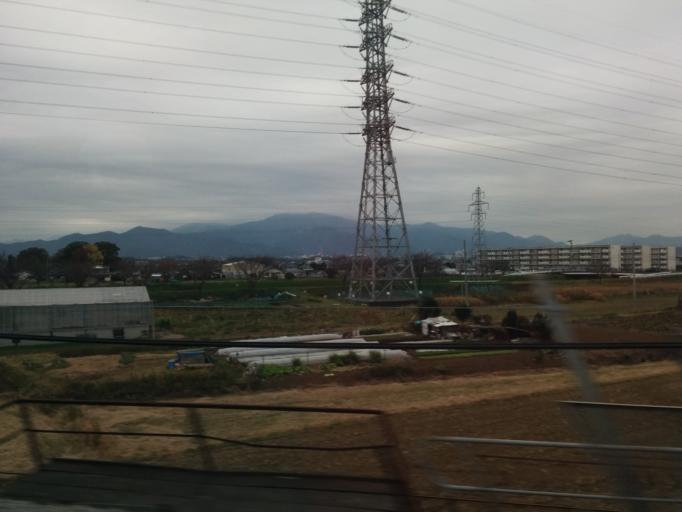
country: JP
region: Kanagawa
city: Isehara
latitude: 35.3756
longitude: 139.3481
